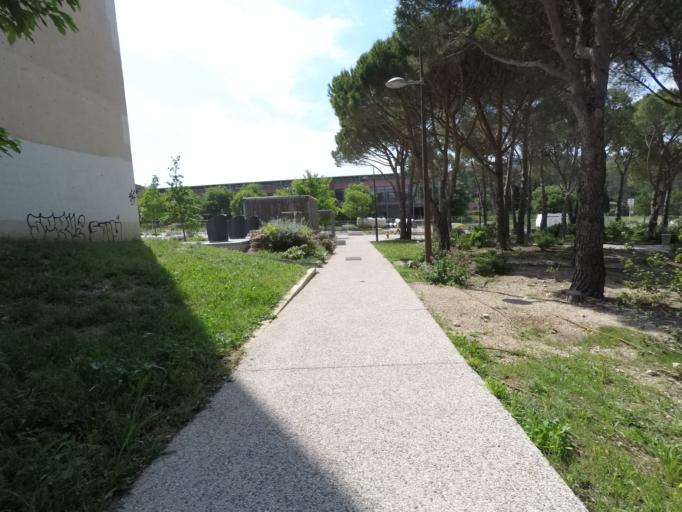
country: FR
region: Provence-Alpes-Cote d'Azur
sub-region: Departement des Bouches-du-Rhone
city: Marseille 09
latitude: 43.2316
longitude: 5.4392
